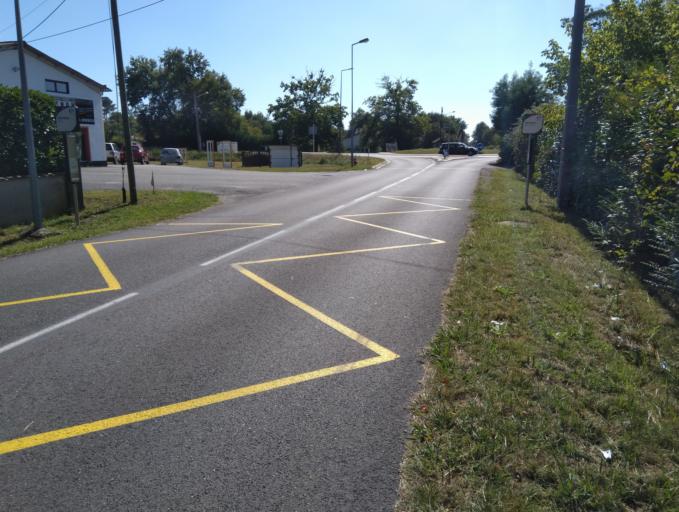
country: FR
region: Aquitaine
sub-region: Departement des Landes
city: Narrosse
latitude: 43.6889
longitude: -1.0023
